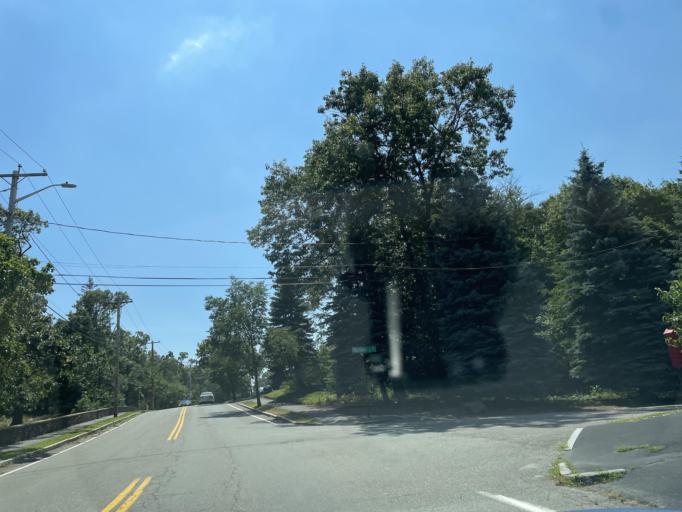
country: US
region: Massachusetts
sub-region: Norfolk County
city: Quincy
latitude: 42.2400
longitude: -70.9972
